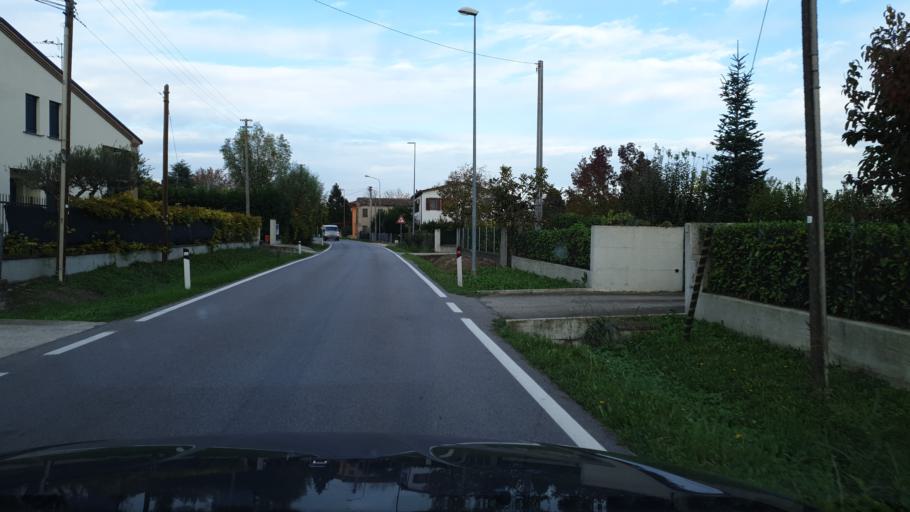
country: IT
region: Veneto
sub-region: Provincia di Padova
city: Conselve
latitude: 45.2249
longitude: 11.8568
